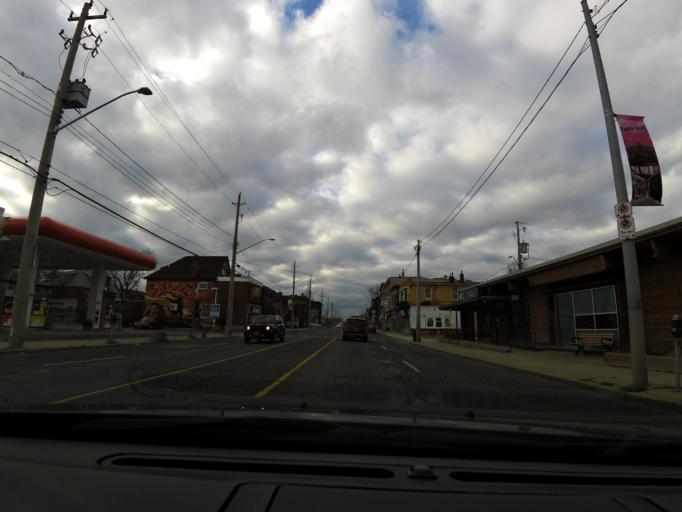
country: CA
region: Ontario
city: Hamilton
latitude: 43.2578
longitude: -79.8411
